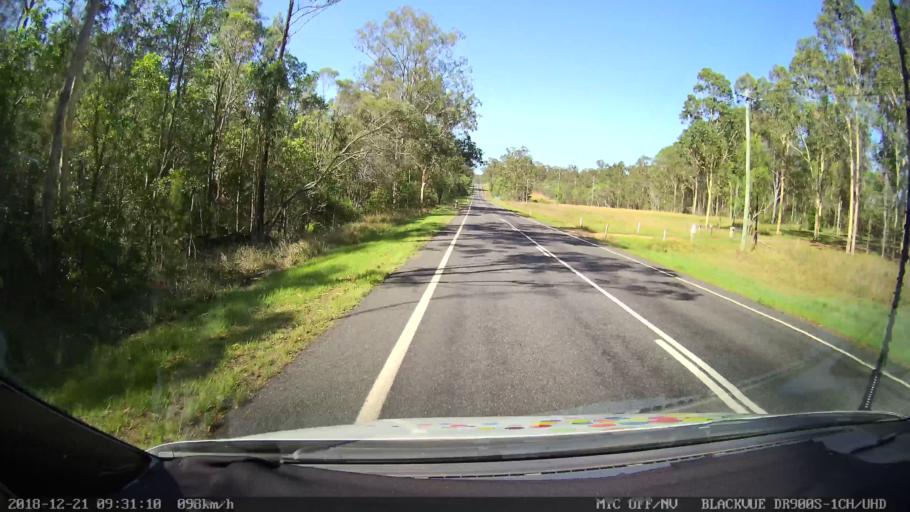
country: AU
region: New South Wales
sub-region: Clarence Valley
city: Maclean
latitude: -29.4569
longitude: 152.9919
